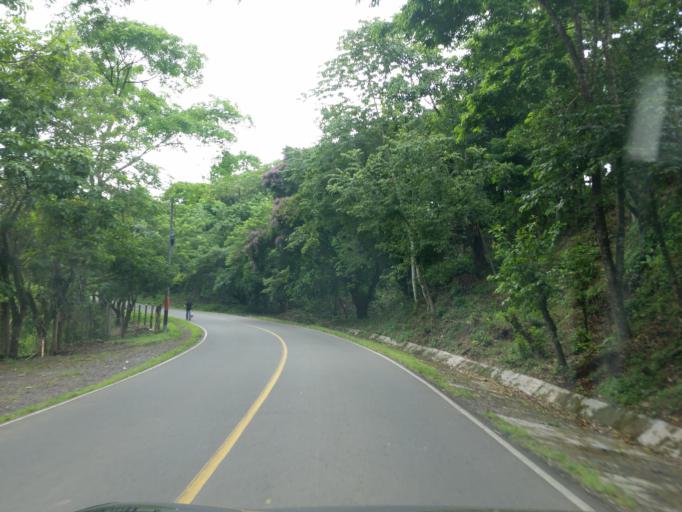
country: NI
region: Matagalpa
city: San Ramon
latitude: 13.0073
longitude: -85.7999
